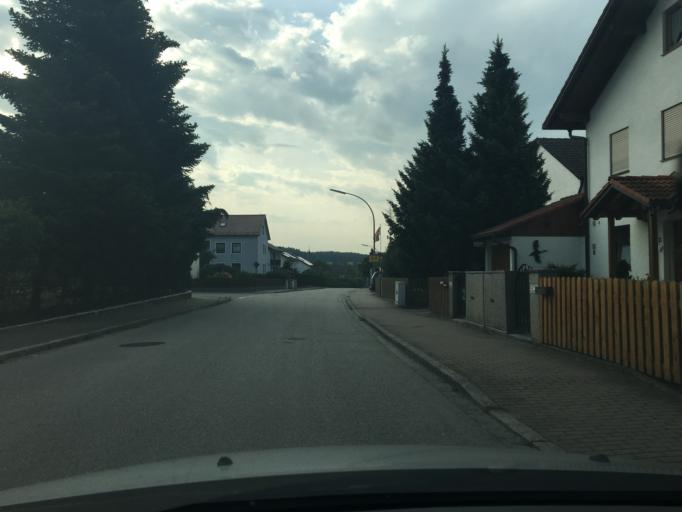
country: DE
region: Bavaria
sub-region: Lower Bavaria
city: Bodenkirchen
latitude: 48.3855
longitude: 12.3817
